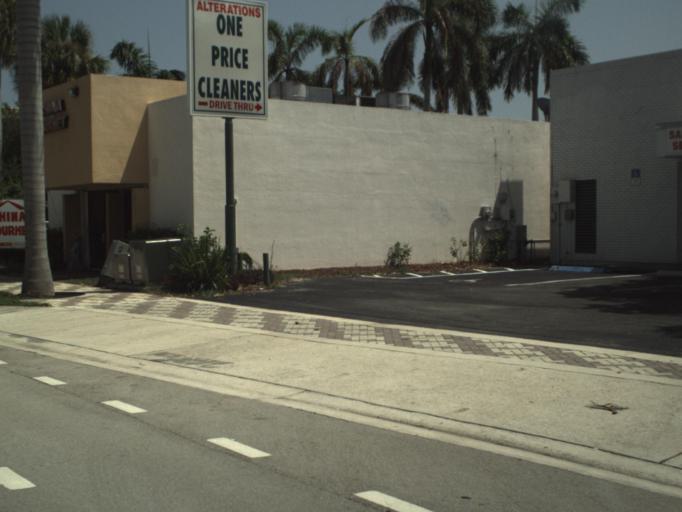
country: US
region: Florida
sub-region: Broward County
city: Deerfield Beach
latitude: 26.3168
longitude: -80.0890
